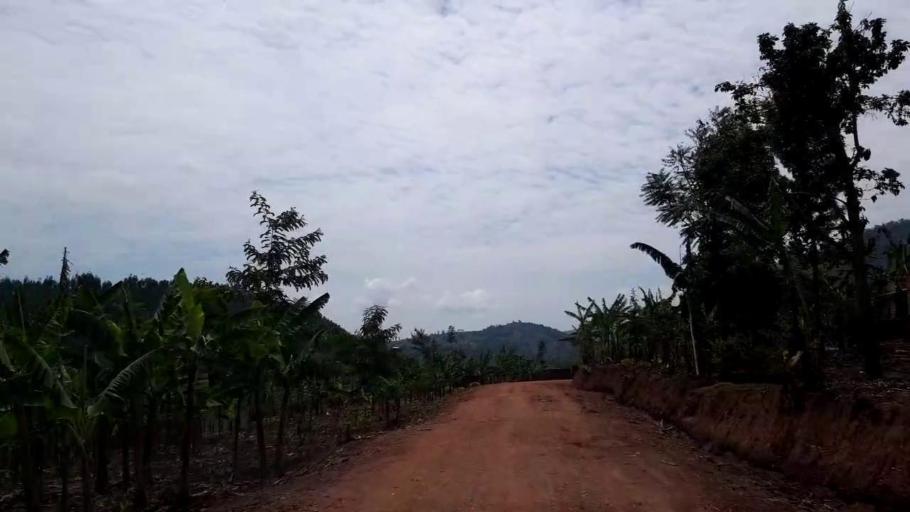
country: RW
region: Northern Province
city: Byumba
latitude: -1.5022
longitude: 30.1929
